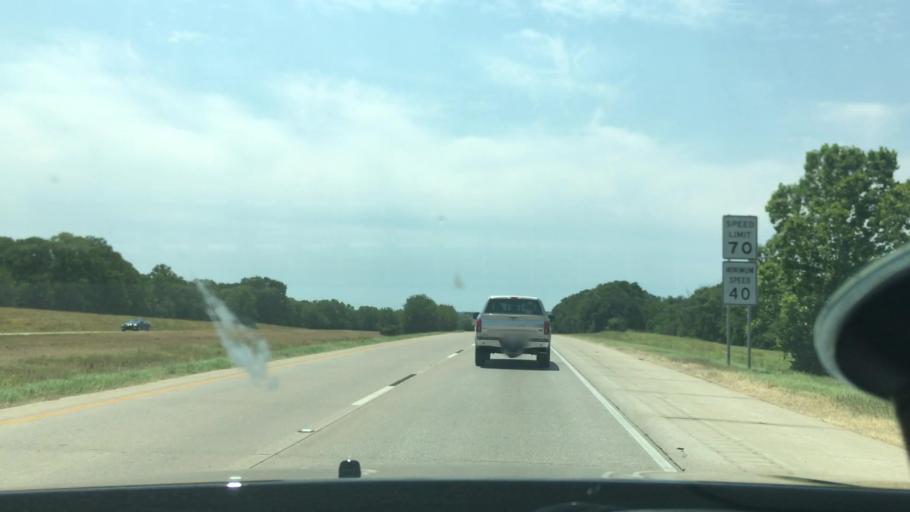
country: US
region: Oklahoma
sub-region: Carter County
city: Ardmore
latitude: 34.0623
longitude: -97.1497
